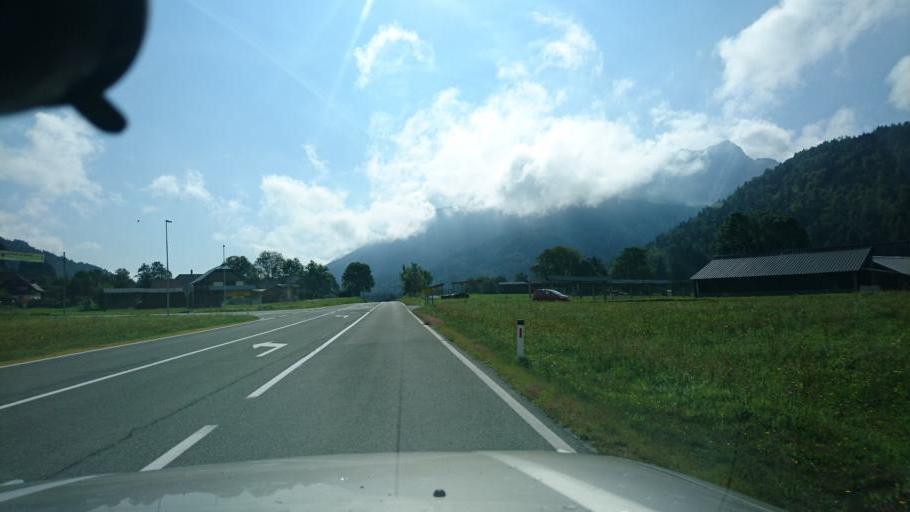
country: AT
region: Carinthia
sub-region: Politischer Bezirk Villach Land
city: Arnoldstein
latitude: 46.4964
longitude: 13.7103
